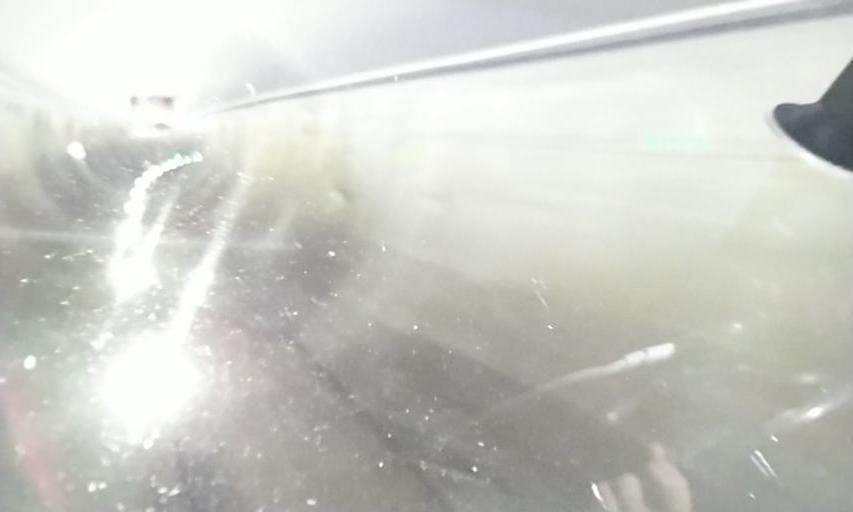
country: PT
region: Castelo Branco
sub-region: Concelho do Fundao
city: Fundao
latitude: 40.1052
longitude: -7.4689
